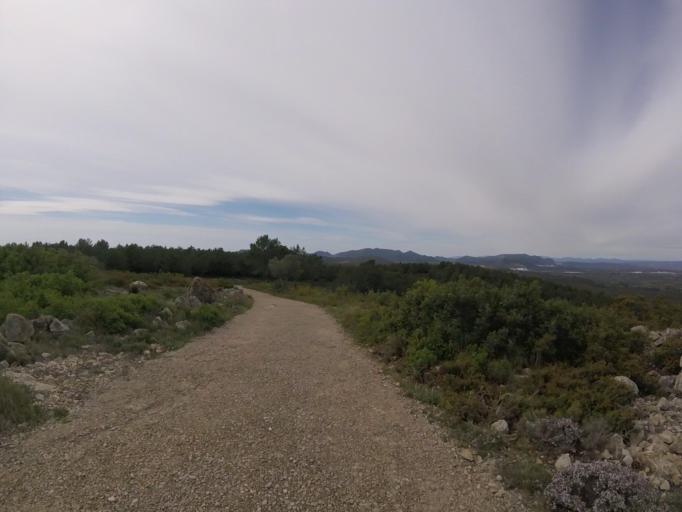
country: ES
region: Valencia
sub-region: Provincia de Castello
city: Cabanes
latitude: 40.1897
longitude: 0.0810
